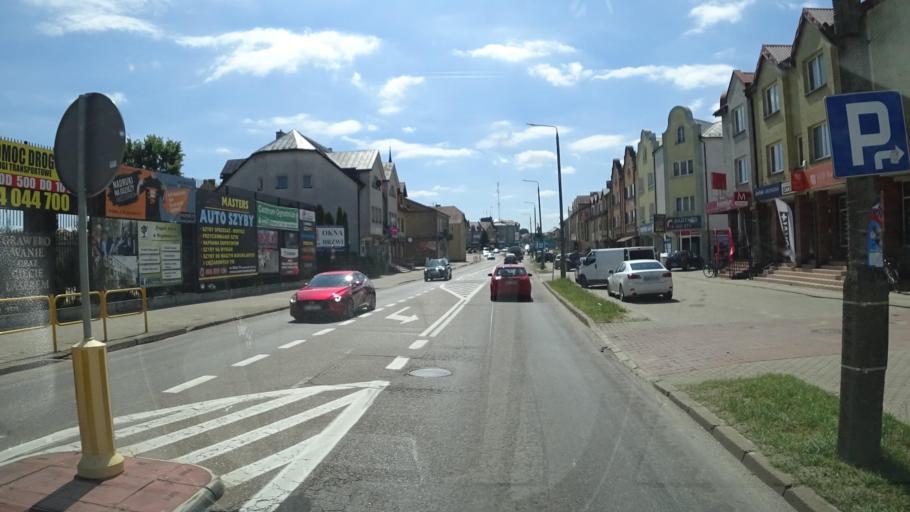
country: PL
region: Podlasie
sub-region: Powiat grajewski
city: Grajewo
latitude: 53.6495
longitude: 22.4551
